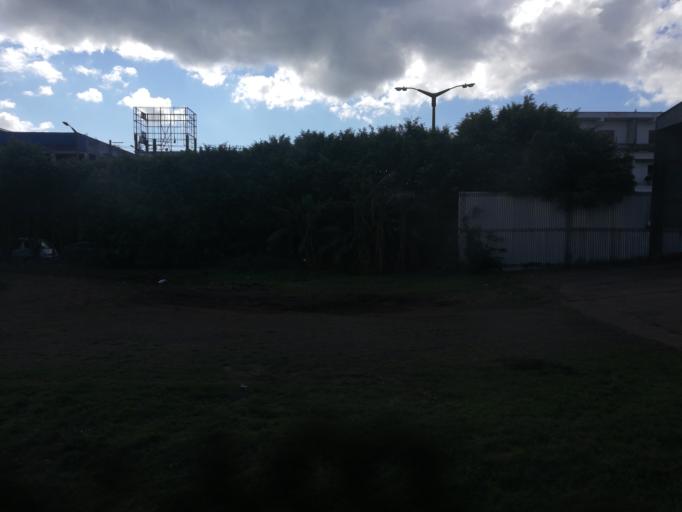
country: PY
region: Itapua
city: Encarnacion
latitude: -27.3618
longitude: -55.8496
